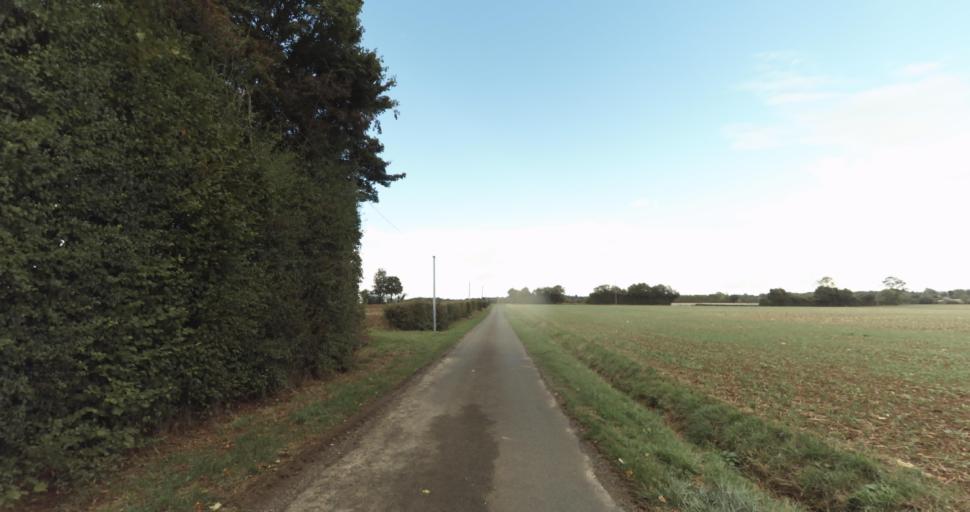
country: FR
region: Lower Normandy
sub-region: Departement de l'Orne
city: Sainte-Gauburge-Sainte-Colombe
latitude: 48.7420
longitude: 0.4062
